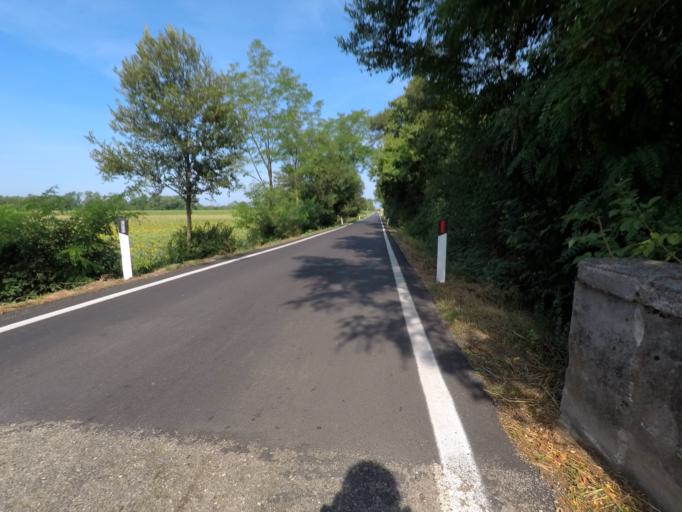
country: IT
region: Friuli Venezia Giulia
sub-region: Provincia di Udine
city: San Vito di Fagagna
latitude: 46.0658
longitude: 13.0942
